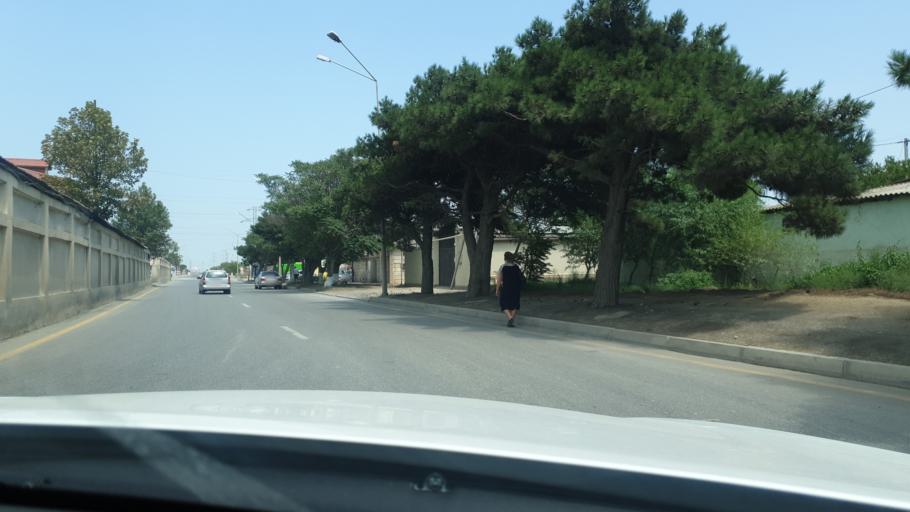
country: AZ
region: Baki
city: Qaracuxur
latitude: 40.3946
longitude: 49.9980
